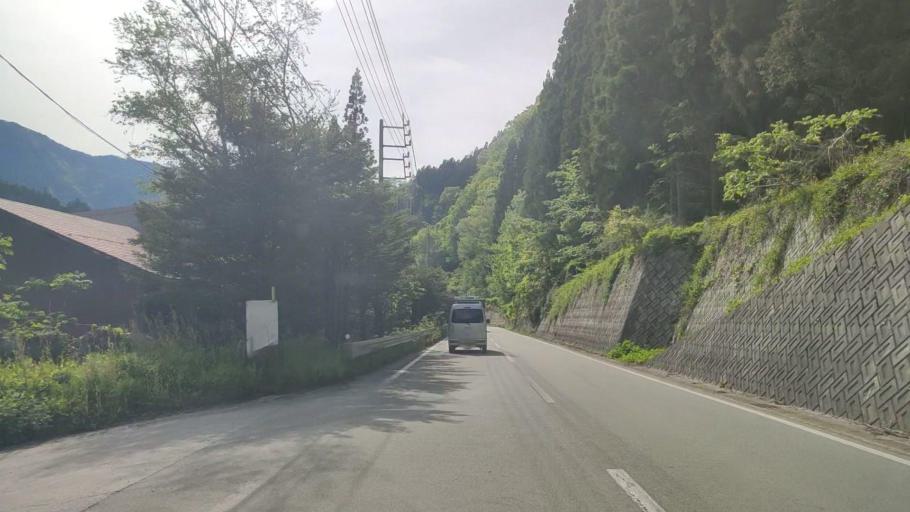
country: JP
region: Gifu
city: Takayama
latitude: 36.2601
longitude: 137.4536
